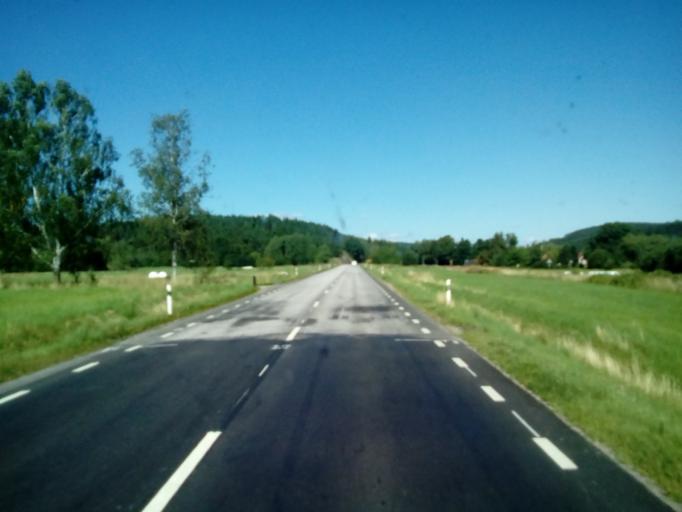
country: SE
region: OEstergoetland
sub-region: Kinda Kommun
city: Kisa
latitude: 58.0073
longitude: 15.6445
